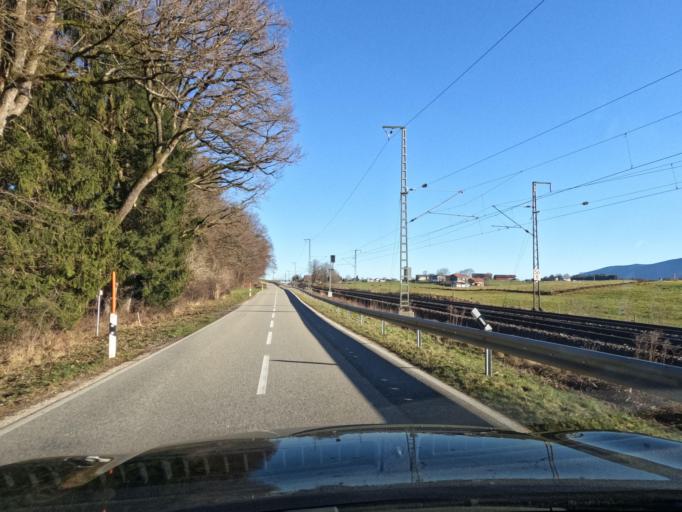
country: DE
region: Bavaria
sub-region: Upper Bavaria
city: Surberg
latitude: 47.8762
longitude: 12.6808
